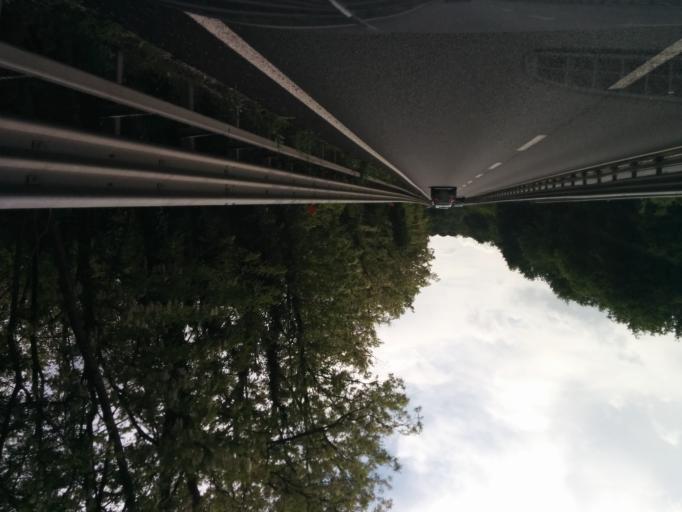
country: IT
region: Tuscany
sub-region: Province of Florence
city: Sambuca
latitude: 43.5432
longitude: 11.2158
